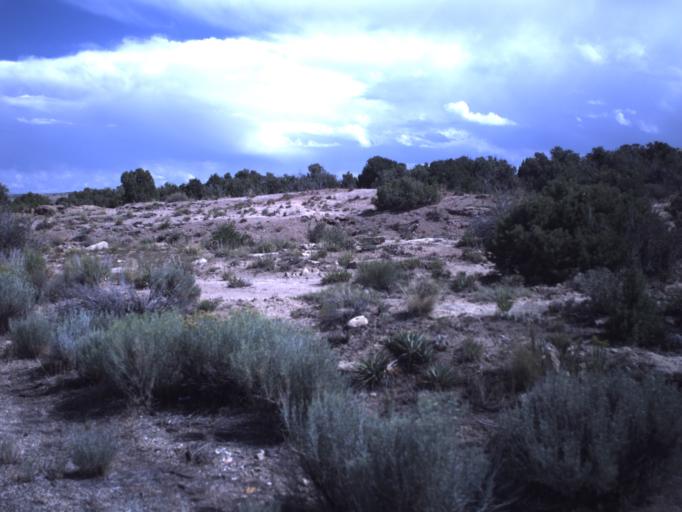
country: US
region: Utah
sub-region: Duchesne County
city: Duchesne
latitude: 40.1770
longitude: -110.4467
